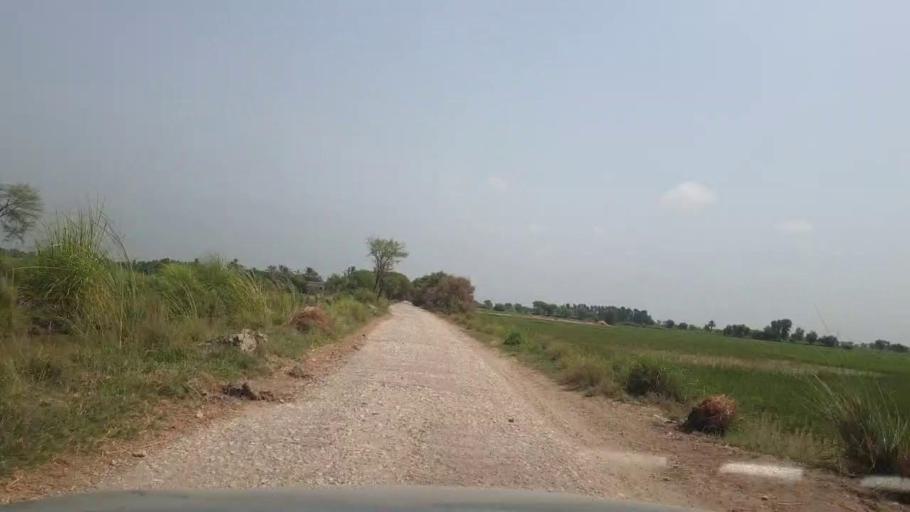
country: PK
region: Sindh
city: Ratodero
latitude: 27.9316
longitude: 68.3634
